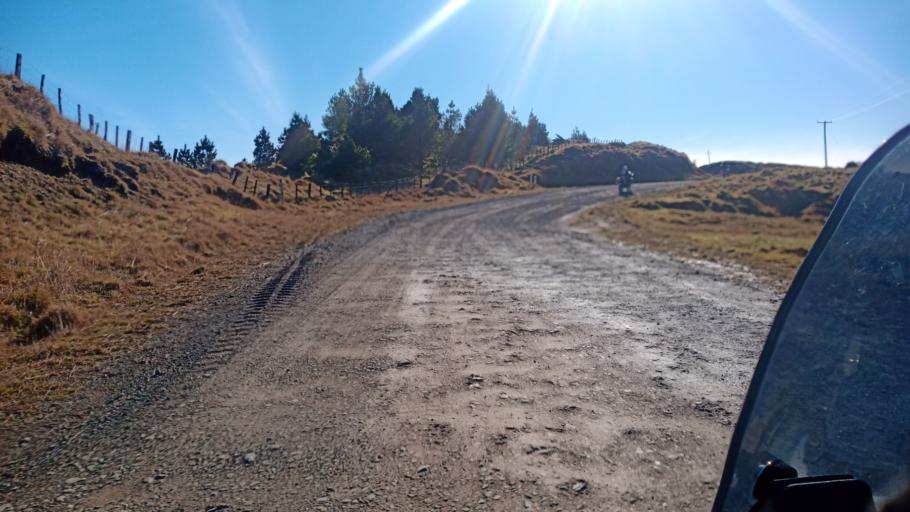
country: NZ
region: Gisborne
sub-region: Gisborne District
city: Gisborne
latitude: -38.1887
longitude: 177.8185
